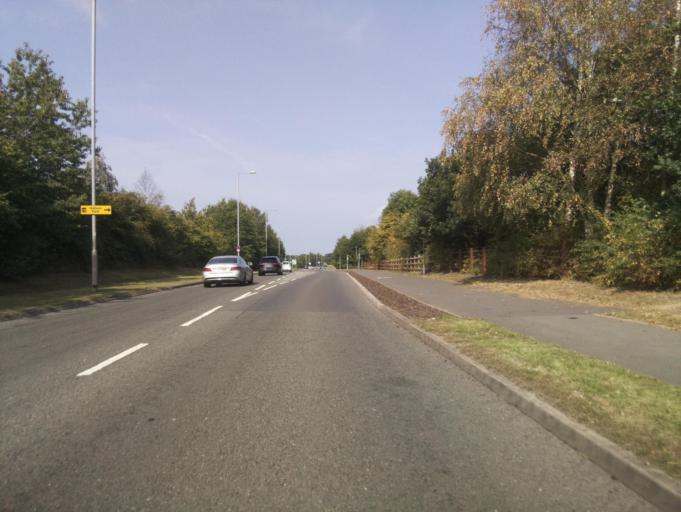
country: GB
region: England
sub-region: Staffordshire
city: Lichfield
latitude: 52.6745
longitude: -1.8478
